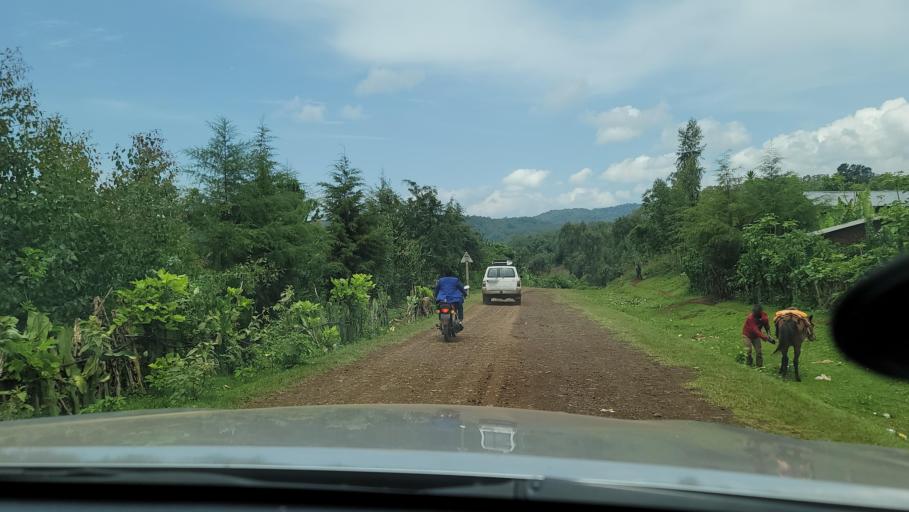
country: ET
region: Southern Nations, Nationalities, and People's Region
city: Bonga
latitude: 7.6999
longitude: 36.2493
